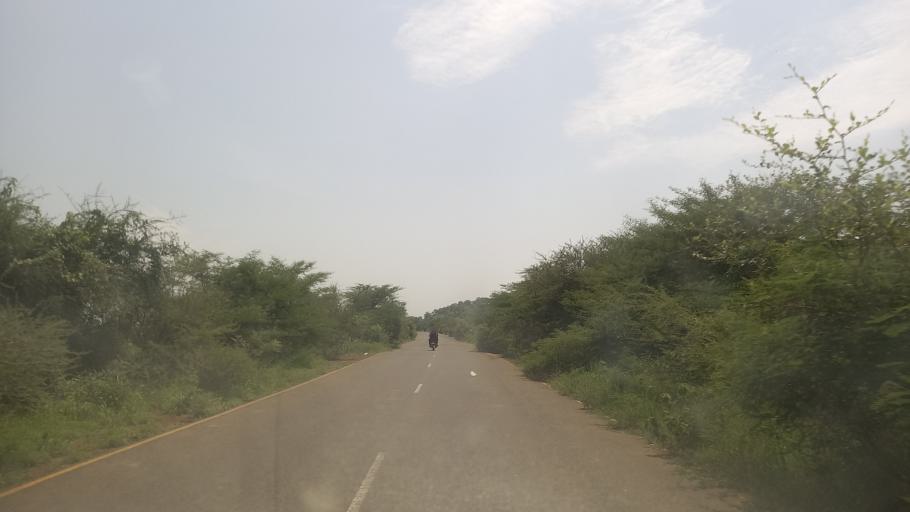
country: ET
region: Gambela
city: Gambela
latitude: 8.2826
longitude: 34.2198
